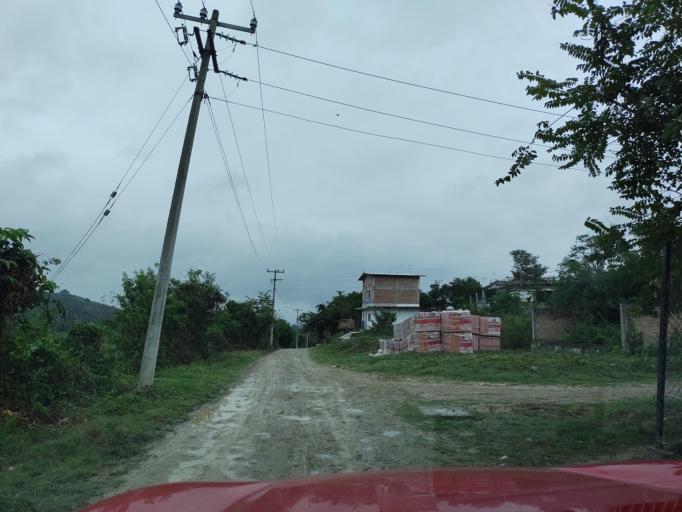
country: MX
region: Veracruz
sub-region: Papantla
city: El Chote
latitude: 20.3970
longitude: -97.3156
